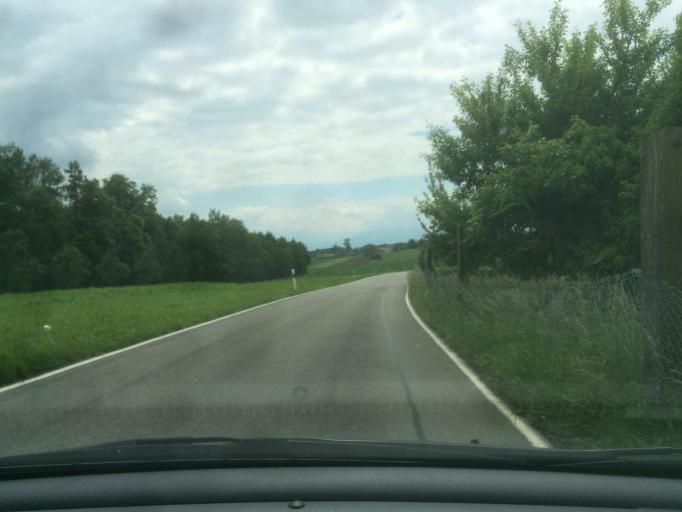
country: CH
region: Zurich
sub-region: Bezirk Pfaeffikon
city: Pfaeffikon / Pfaeffikon (Dorfkern)
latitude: 47.3529
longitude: 8.7674
